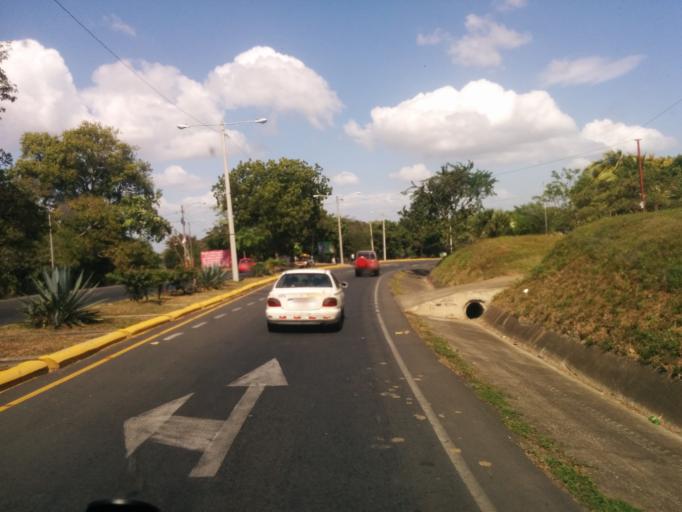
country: NI
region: Masaya
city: Masaya
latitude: 11.9558
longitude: -86.0918
